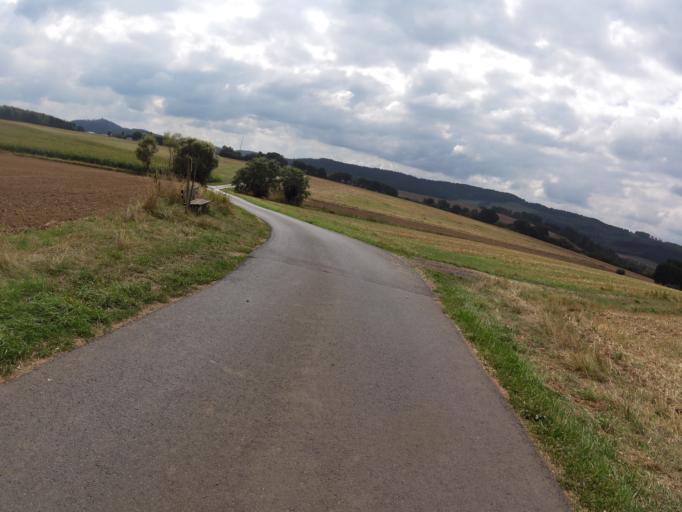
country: DE
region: Rheinland-Pfalz
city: Oberbettingen
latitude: 50.2816
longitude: 6.6471
